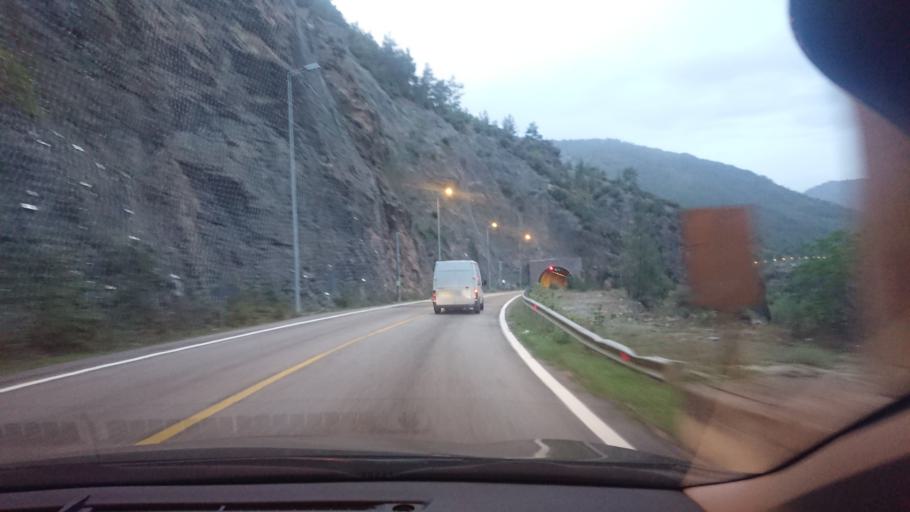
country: TR
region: Karabuk
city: Karabuk
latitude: 41.1532
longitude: 32.5236
